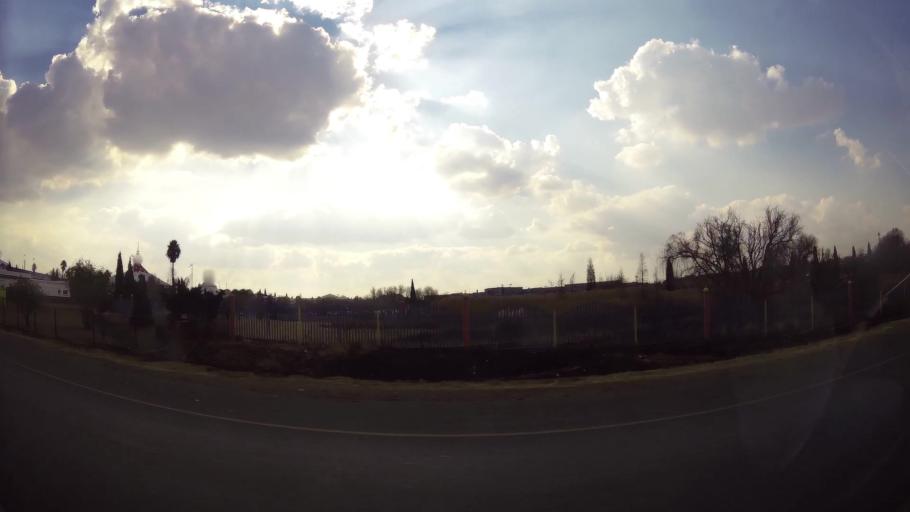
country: ZA
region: Gauteng
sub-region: Ekurhuleni Metropolitan Municipality
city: Brakpan
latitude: -26.2595
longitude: 28.3193
